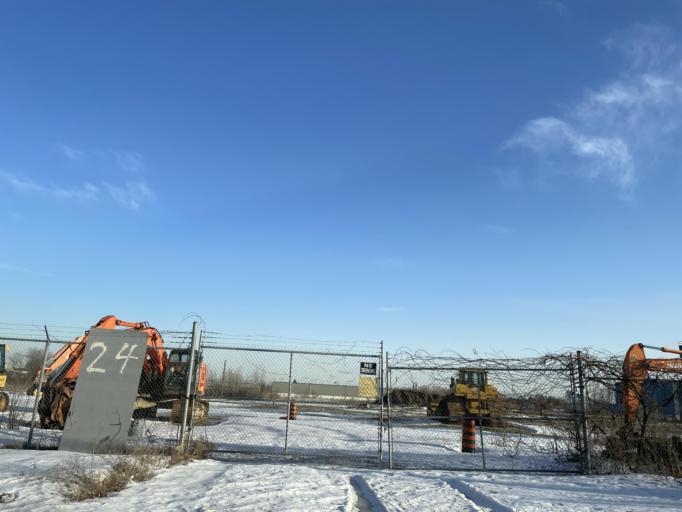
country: CA
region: Ontario
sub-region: Wellington County
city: Guelph
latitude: 43.5525
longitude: -80.2855
